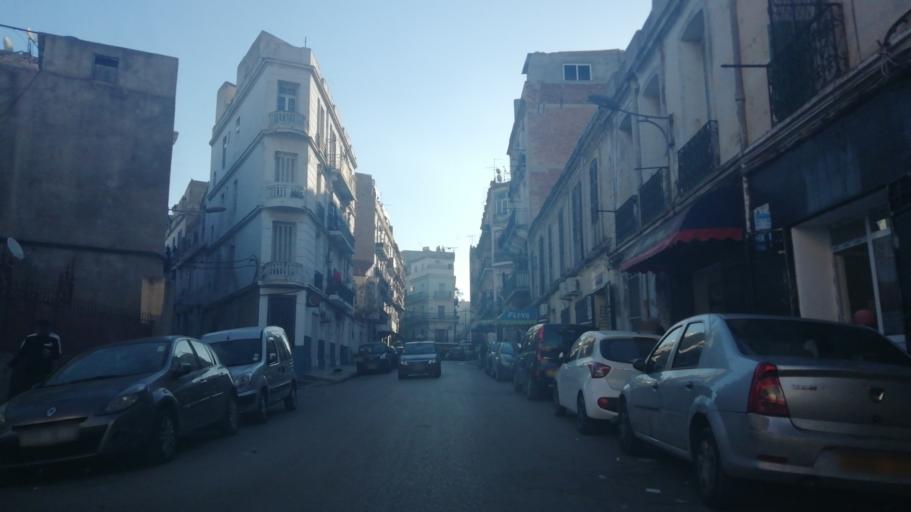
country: DZ
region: Oran
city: Oran
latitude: 35.7014
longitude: -0.6382
